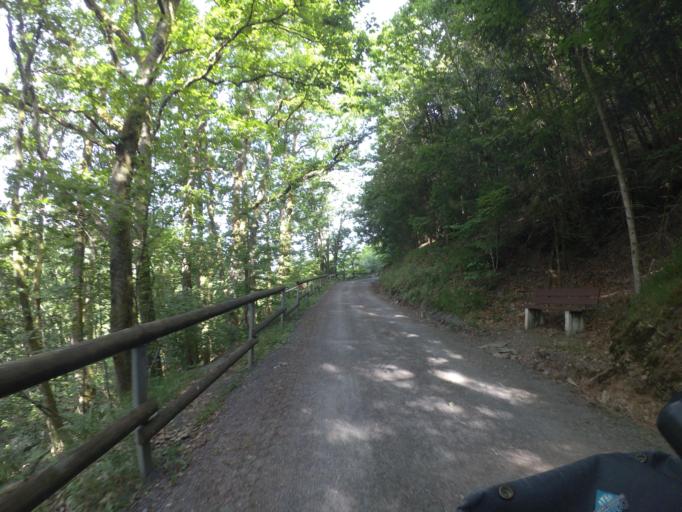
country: DE
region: Saarland
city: Nonnweiler
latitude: 49.6167
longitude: 6.9437
